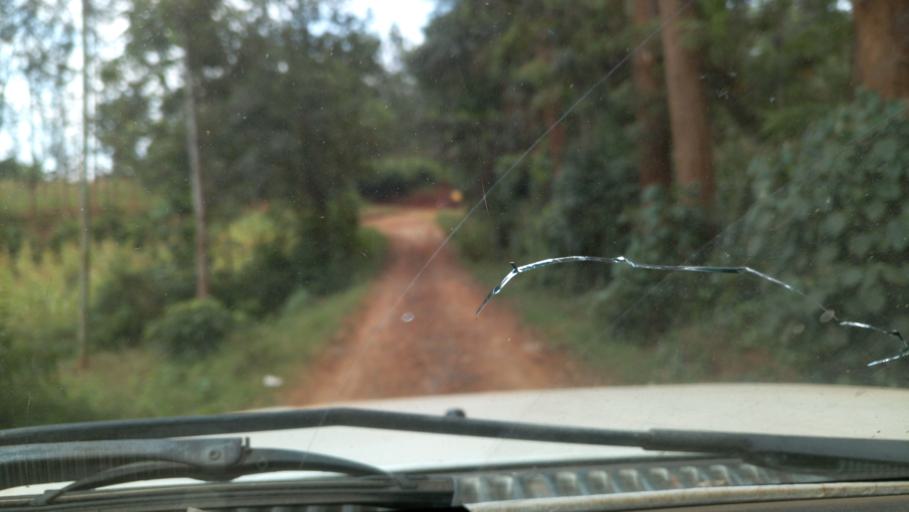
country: KE
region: Murang'a District
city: Murang'a
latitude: -0.6588
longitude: 37.1050
